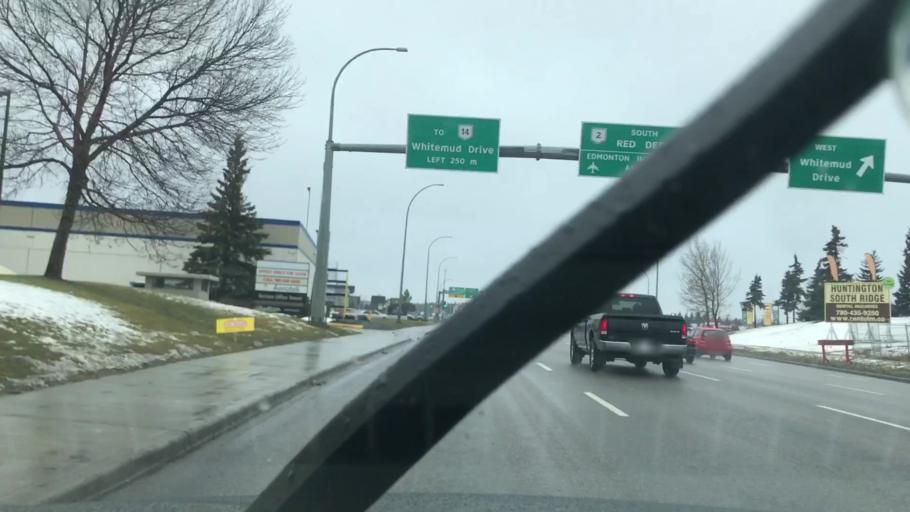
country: CA
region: Alberta
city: Edmonton
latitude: 53.4825
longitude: -113.4950
